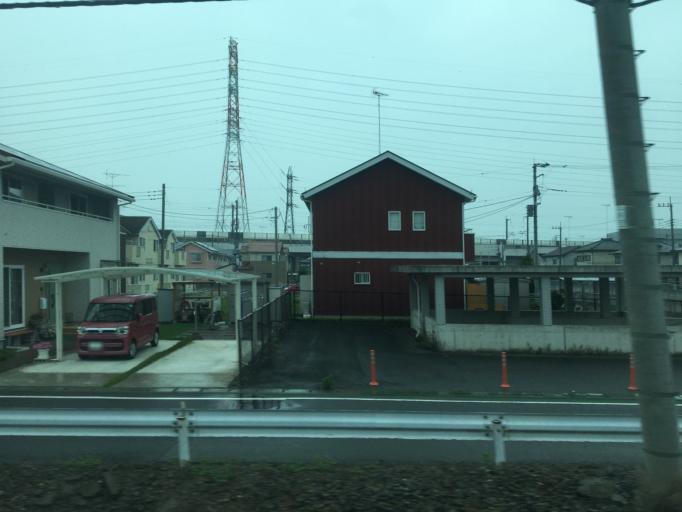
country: JP
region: Tochigi
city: Oyama
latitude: 36.2727
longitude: 139.7738
